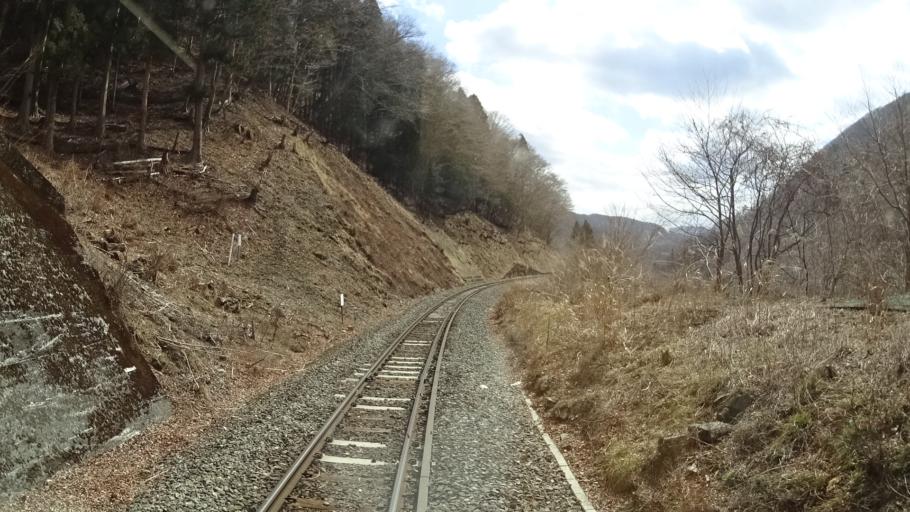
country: JP
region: Iwate
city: Tono
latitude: 39.2428
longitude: 141.6709
